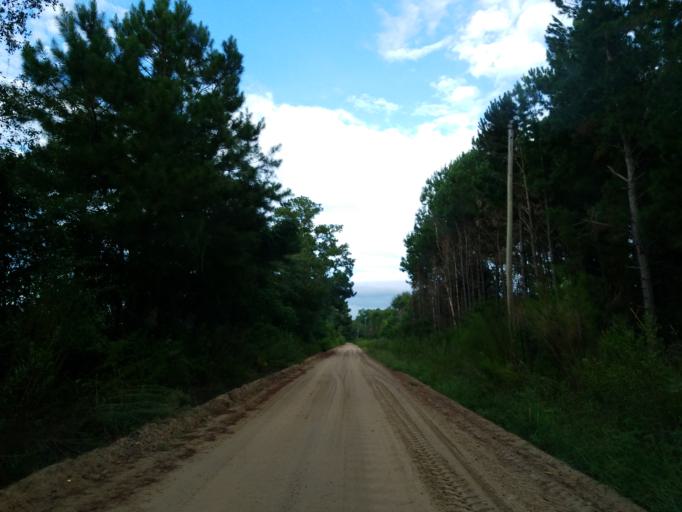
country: US
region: Georgia
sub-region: Cook County
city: Sparks
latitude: 31.2354
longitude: -83.4437
